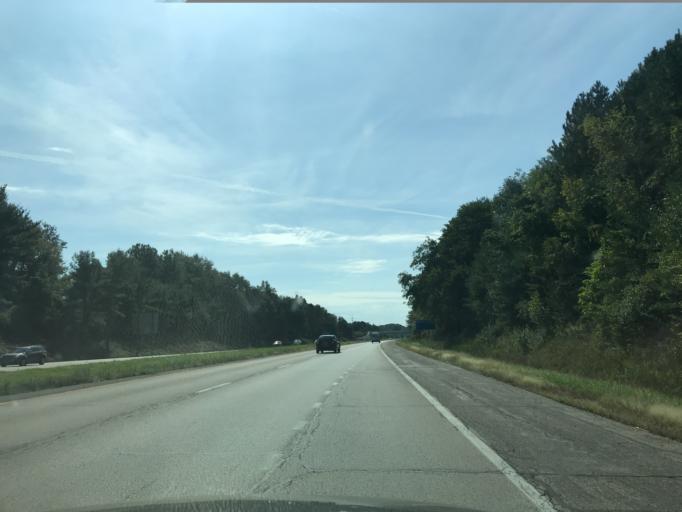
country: US
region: Ohio
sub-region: Ashtabula County
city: Edgewood
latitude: 41.8713
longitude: -80.7613
